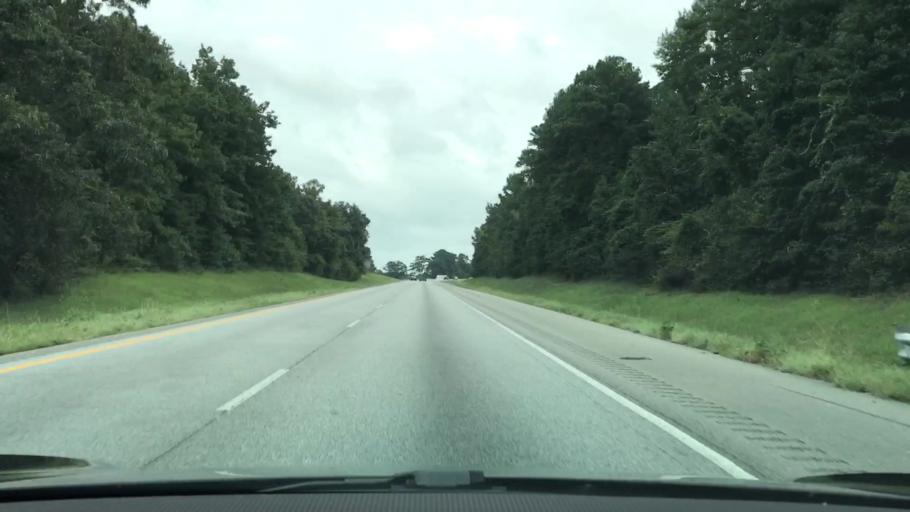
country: US
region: Alabama
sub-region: Lee County
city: Auburn
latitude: 32.5241
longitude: -85.5716
